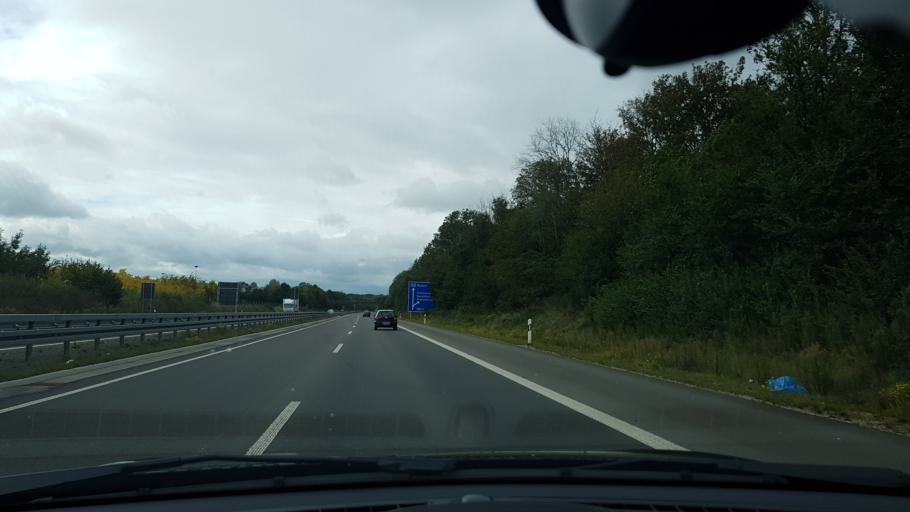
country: DE
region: North Rhine-Westphalia
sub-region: Regierungsbezirk Dusseldorf
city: Grevenbroich
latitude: 51.0750
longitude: 6.6098
